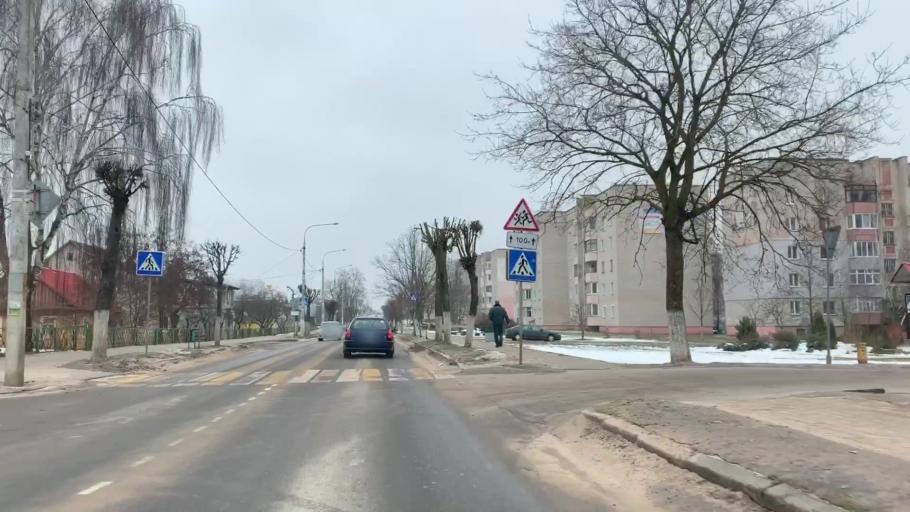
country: BY
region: Minsk
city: Nyasvizh
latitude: 53.2259
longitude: 26.6686
